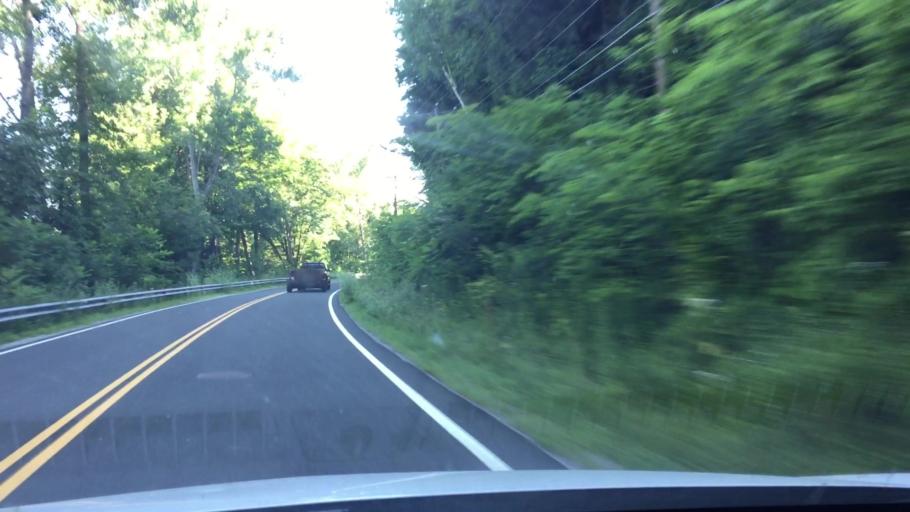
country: US
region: Massachusetts
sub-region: Berkshire County
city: Lee
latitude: 42.2820
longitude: -73.2400
